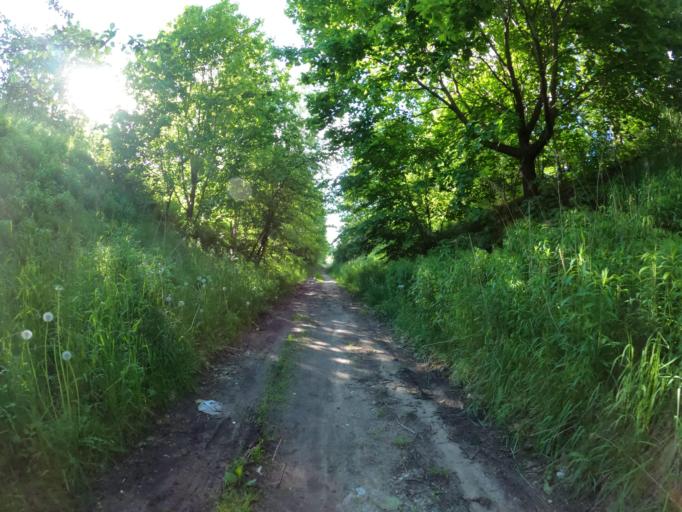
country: PL
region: Warmian-Masurian Voivodeship
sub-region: Powiat lidzbarski
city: Lidzbark Warminski
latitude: 54.1263
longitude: 20.5965
